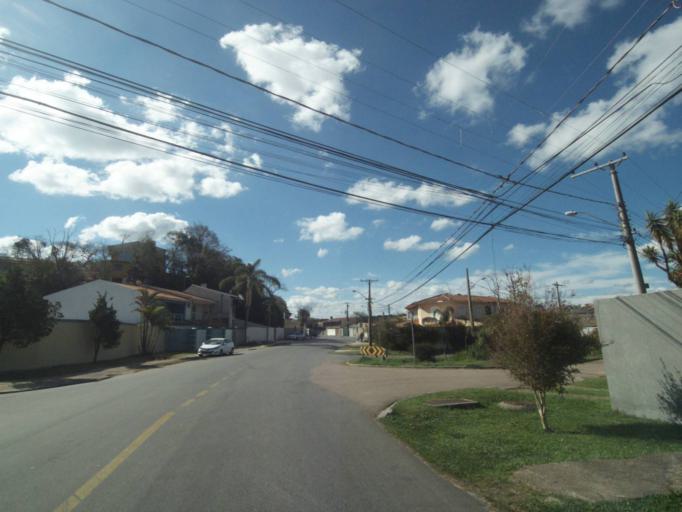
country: BR
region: Parana
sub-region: Curitiba
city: Curitiba
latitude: -25.3838
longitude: -49.2483
